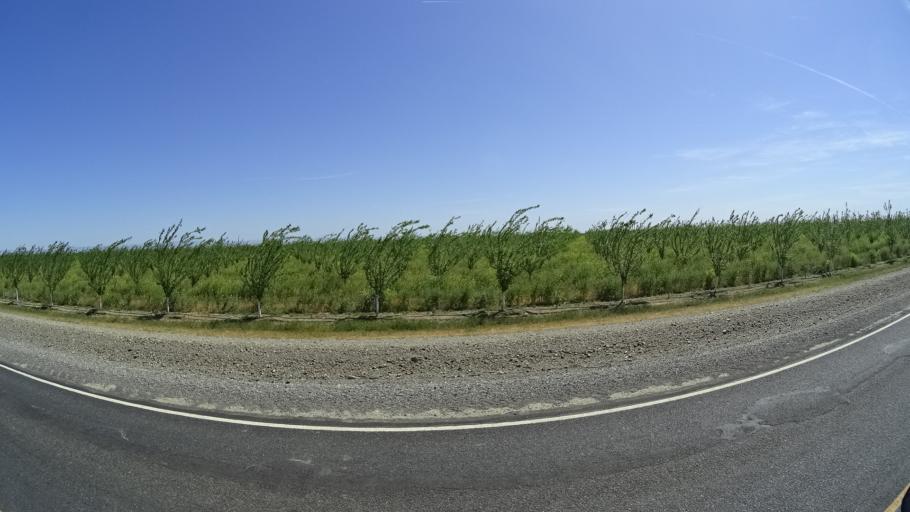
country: US
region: California
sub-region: Glenn County
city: Orland
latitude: 39.6540
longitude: -122.1408
